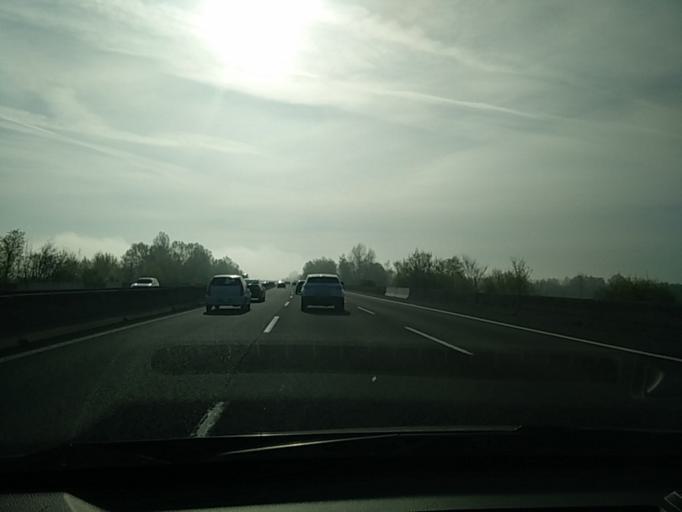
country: IT
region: Emilia-Romagna
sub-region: Provincia di Bologna
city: Ozzano dell'Emilia
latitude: 44.4607
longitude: 11.5046
